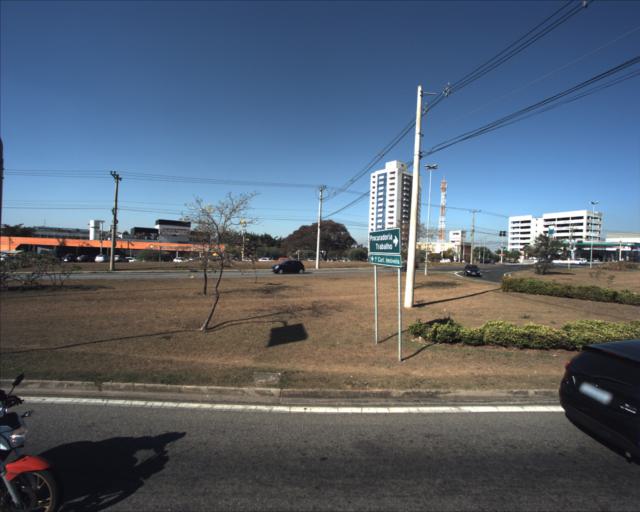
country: BR
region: Sao Paulo
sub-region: Sorocaba
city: Sorocaba
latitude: -23.4726
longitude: -47.4232
